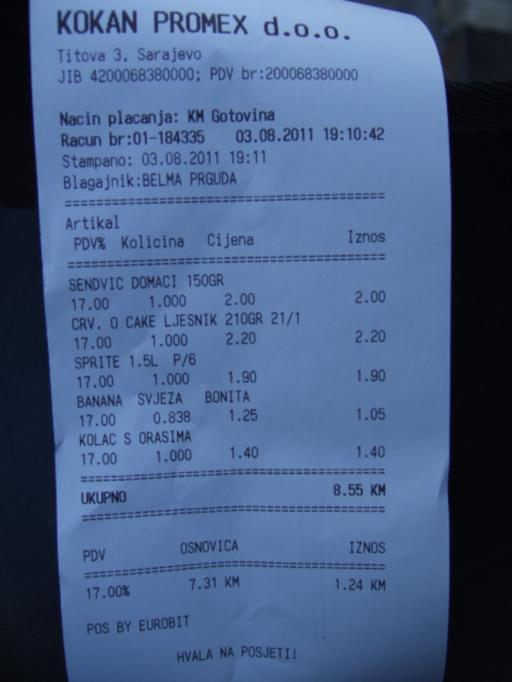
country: BA
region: Federation of Bosnia and Herzegovina
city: Kobilja Glava
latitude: 43.8563
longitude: 18.4085
